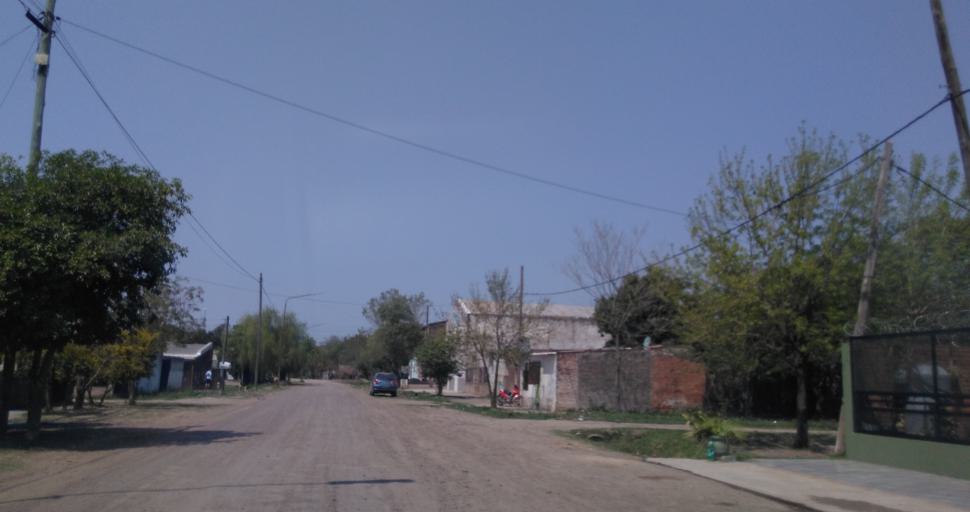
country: AR
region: Chaco
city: Fontana
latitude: -27.4248
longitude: -59.0258
